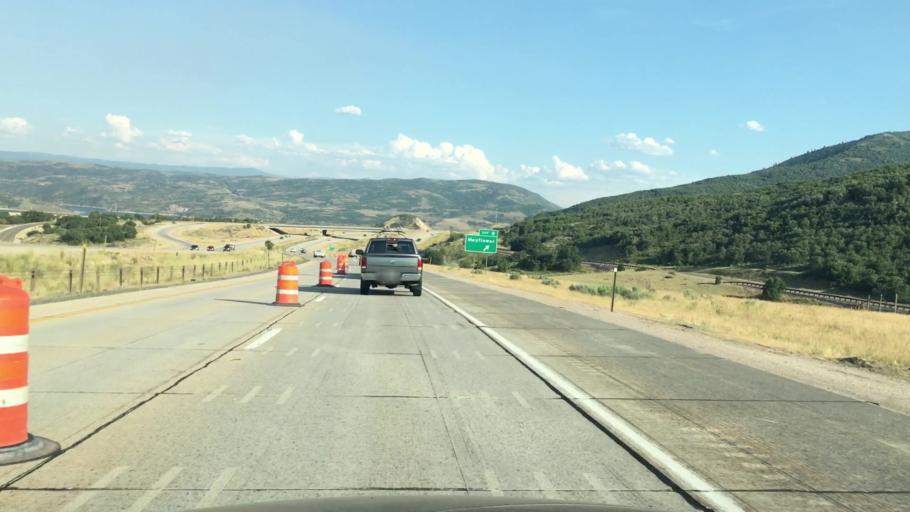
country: US
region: Utah
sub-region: Summit County
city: Park City
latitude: 40.6304
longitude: -111.4466
